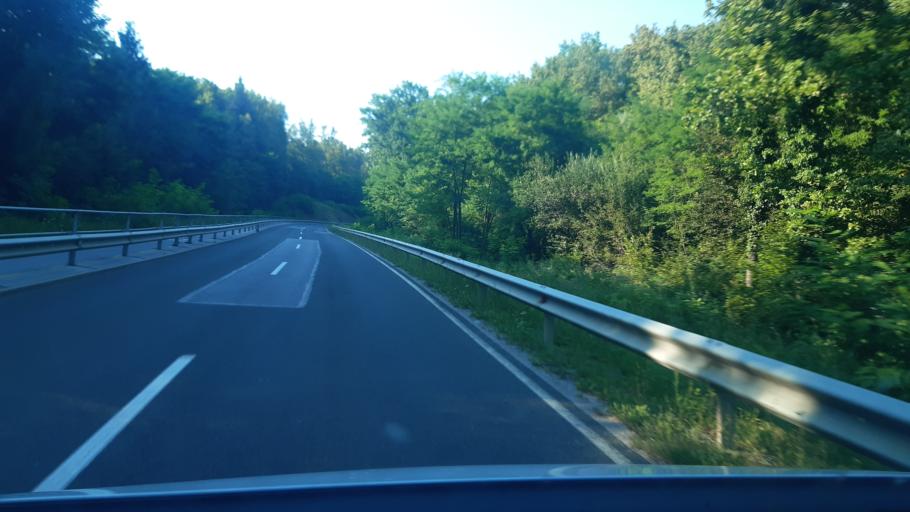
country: SI
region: Crnomelj
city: Crnomelj
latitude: 45.5792
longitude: 15.1816
